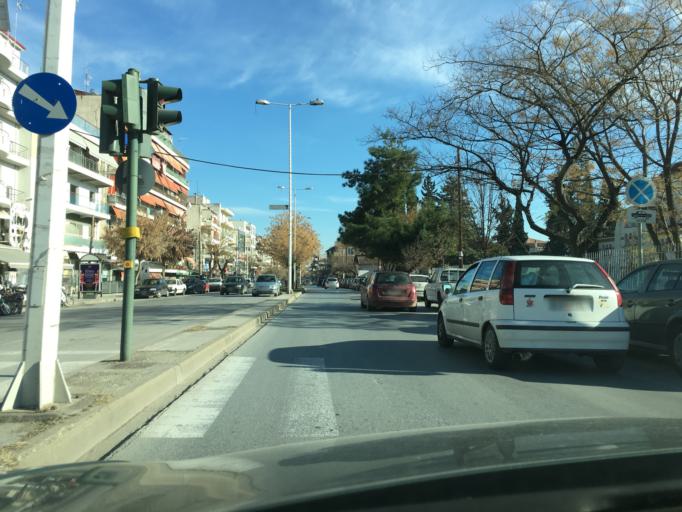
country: GR
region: Thessaly
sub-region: Nomos Larisis
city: Larisa
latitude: 39.6326
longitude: 22.4092
